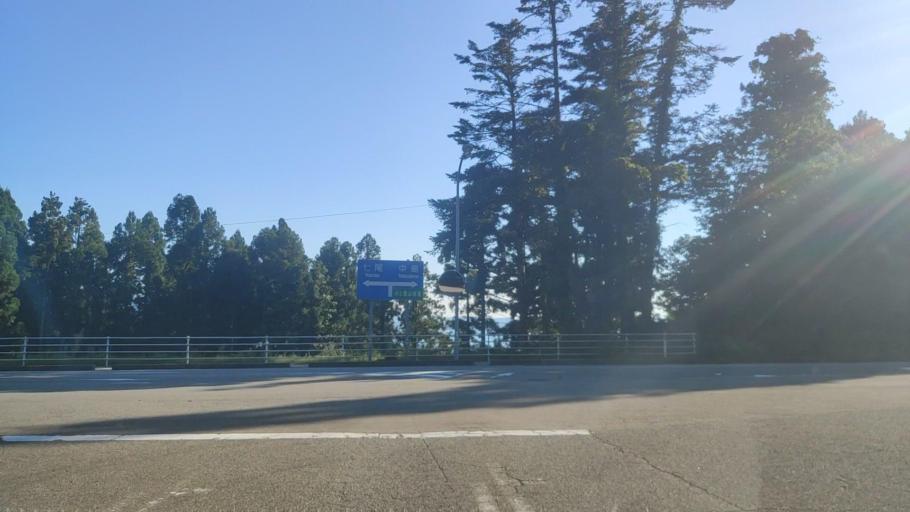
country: JP
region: Ishikawa
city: Nanao
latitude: 37.1191
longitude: 136.9412
